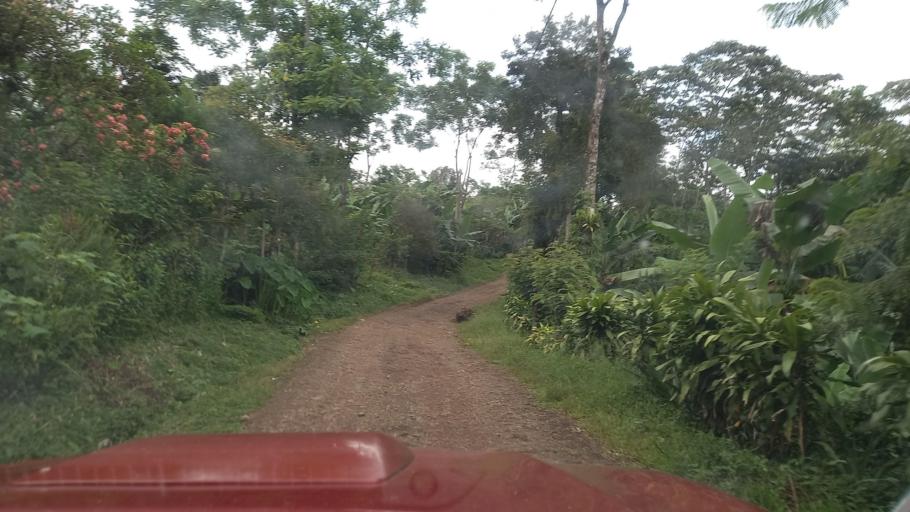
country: NI
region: Jinotega
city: San Jose de Bocay
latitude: 13.3404
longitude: -85.6555
